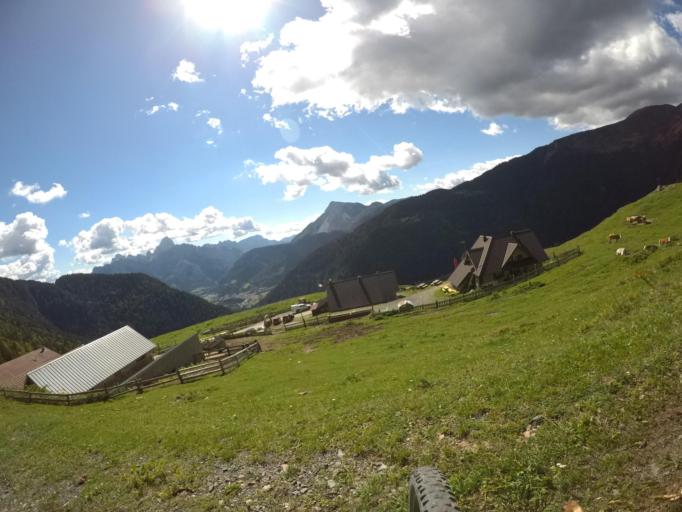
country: IT
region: Friuli Venezia Giulia
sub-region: Provincia di Udine
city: Paularo
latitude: 46.5671
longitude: 13.1220
